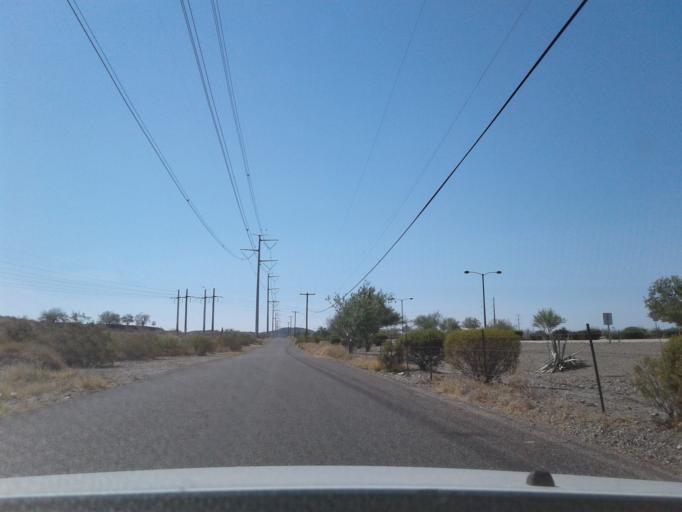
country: US
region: Arizona
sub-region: Maricopa County
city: Laveen
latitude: 33.3235
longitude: -112.1673
